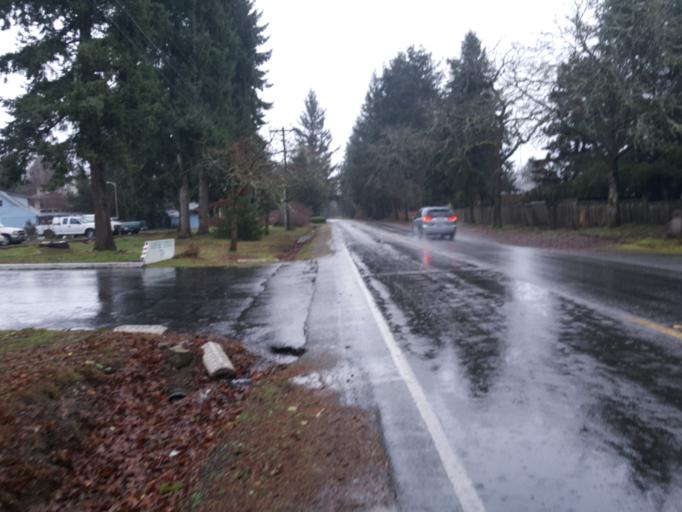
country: US
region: Washington
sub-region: Pierce County
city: Lakewood
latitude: 47.2001
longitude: -122.5353
